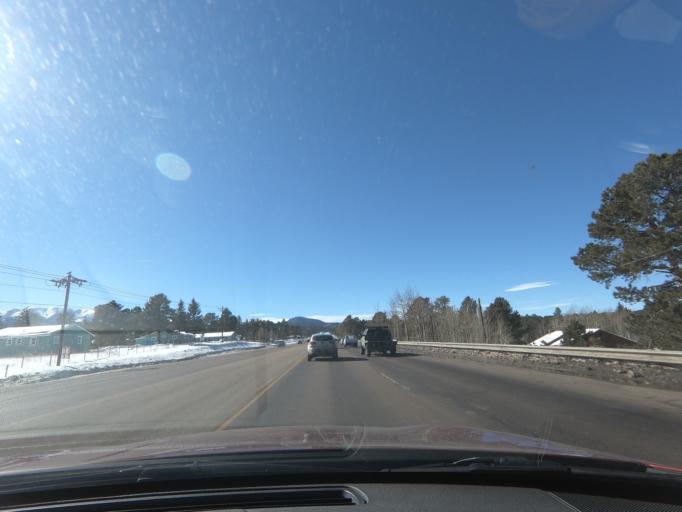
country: US
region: Colorado
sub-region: Teller County
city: Woodland Park
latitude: 38.9714
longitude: -105.0796
